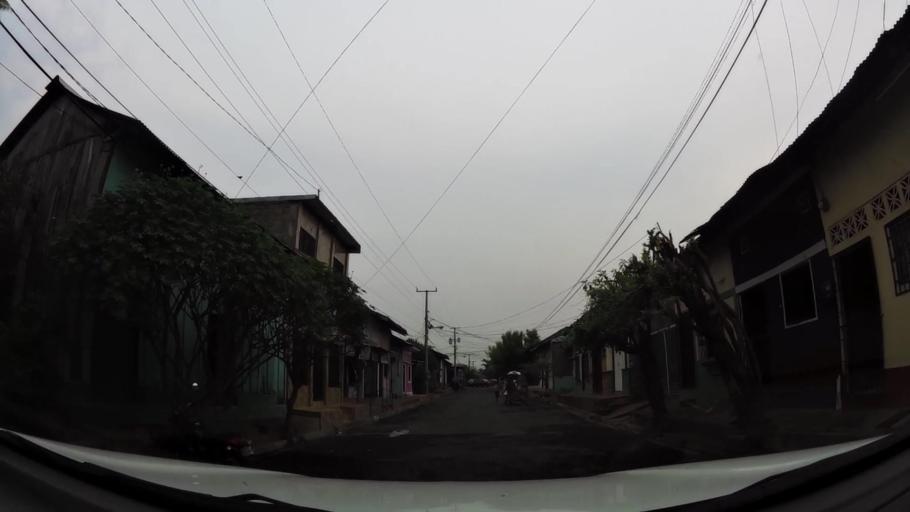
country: NI
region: Leon
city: Leon
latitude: 12.4459
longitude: -86.8769
